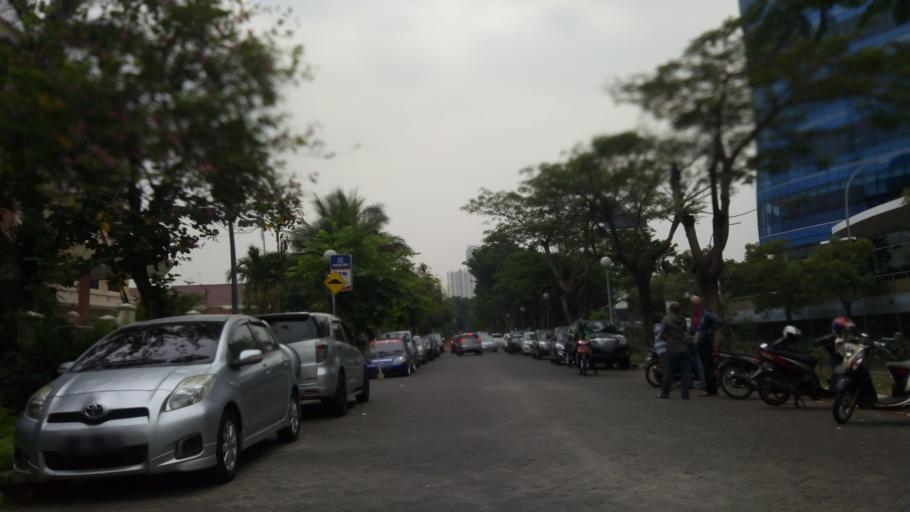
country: ID
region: Jakarta Raya
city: Jakarta
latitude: -6.1534
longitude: 106.8433
